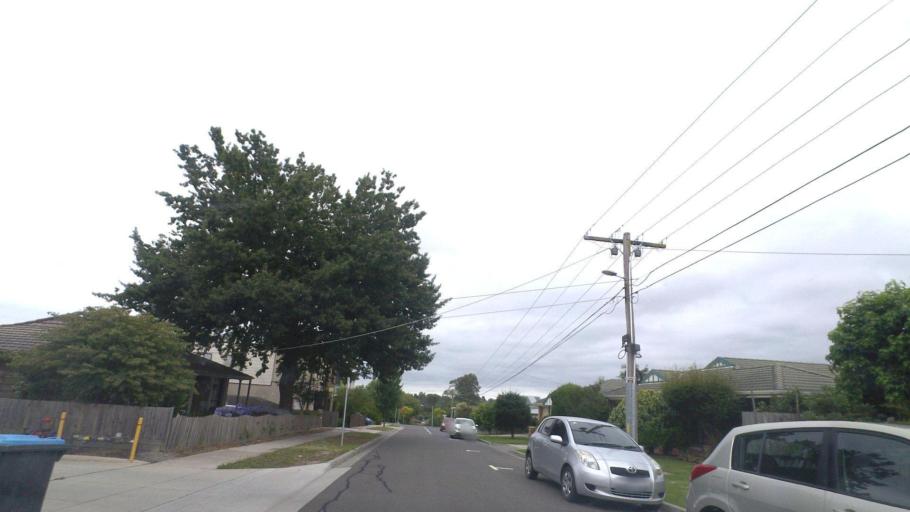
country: AU
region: Victoria
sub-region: Knox
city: Boronia
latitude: -37.8636
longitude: 145.2791
